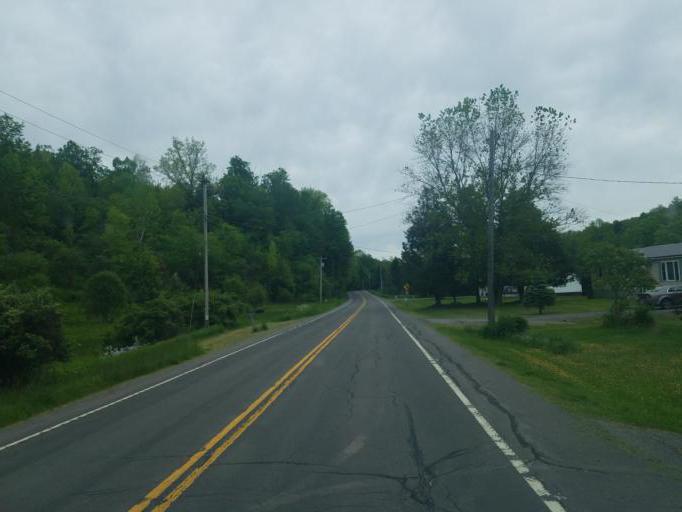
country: US
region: New York
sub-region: Herkimer County
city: Frankfort
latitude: 42.9723
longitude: -75.0999
